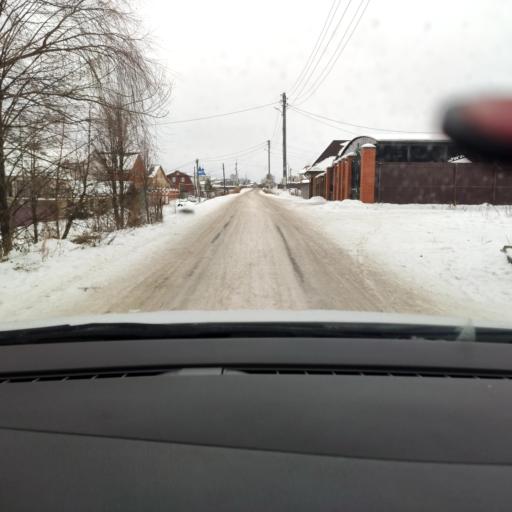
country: RU
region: Tatarstan
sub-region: Gorod Kazan'
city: Kazan
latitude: 55.9001
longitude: 49.1377
